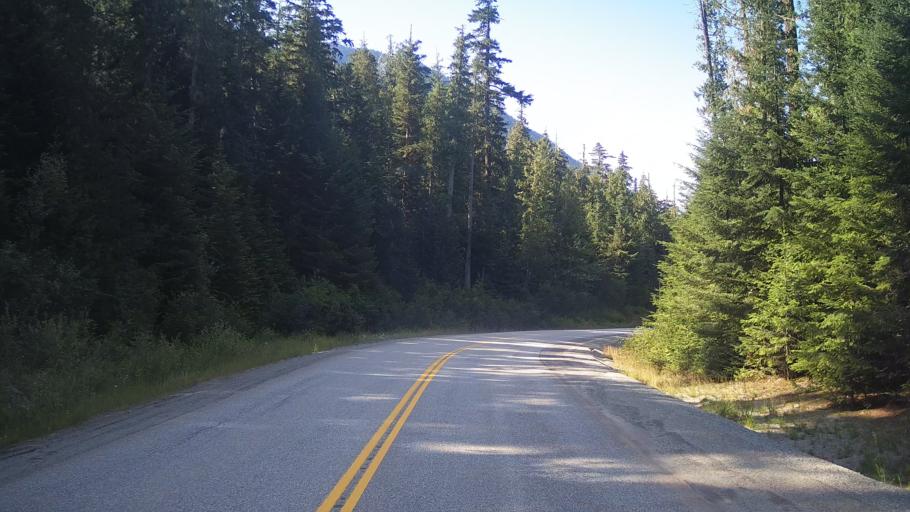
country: CA
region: British Columbia
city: Pemberton
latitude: 50.3465
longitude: -122.5343
